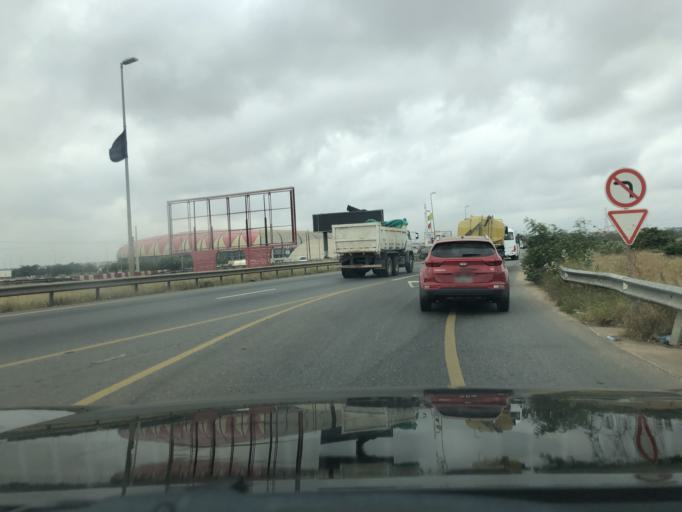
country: AO
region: Luanda
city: Luanda
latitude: -8.9740
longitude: 13.2777
